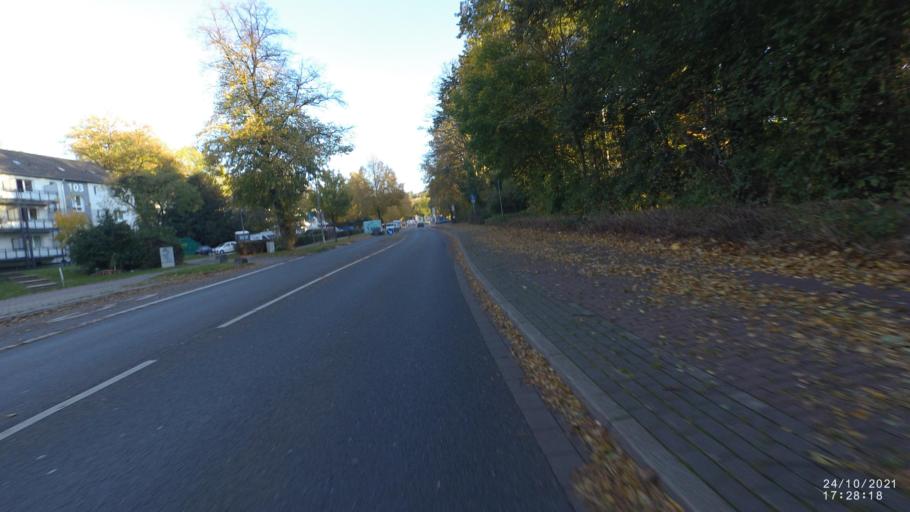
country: DE
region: North Rhine-Westphalia
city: Iserlohn
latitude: 51.3766
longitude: 7.7304
